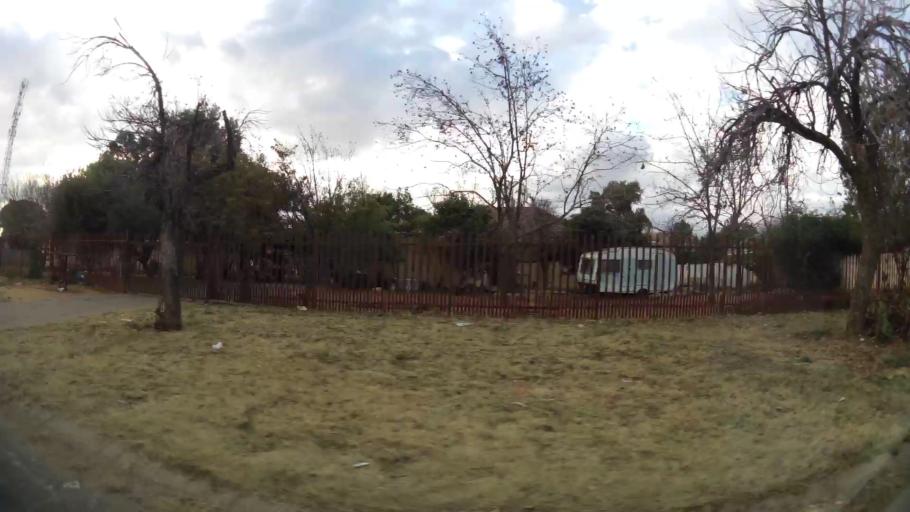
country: ZA
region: Orange Free State
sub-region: Lejweleputswa District Municipality
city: Welkom
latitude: -27.9891
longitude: 26.7154
